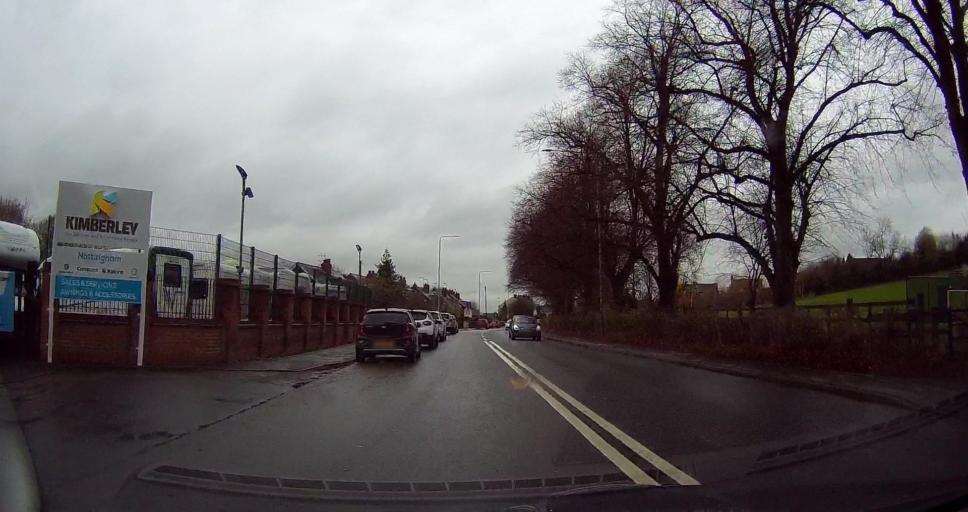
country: GB
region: England
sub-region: Nottinghamshire
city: Kimberley
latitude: 52.9989
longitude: -1.2648
